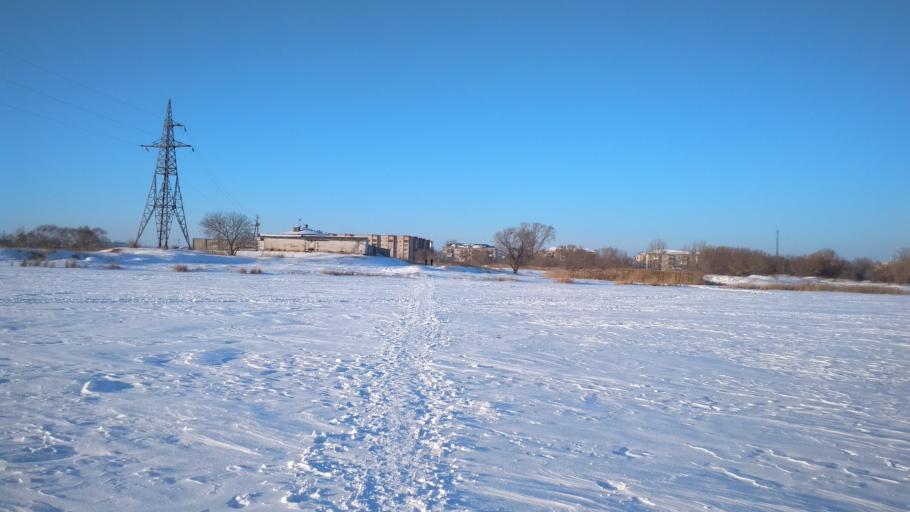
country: RU
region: Chelyabinsk
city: Troitsk
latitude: 54.0808
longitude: 61.5796
